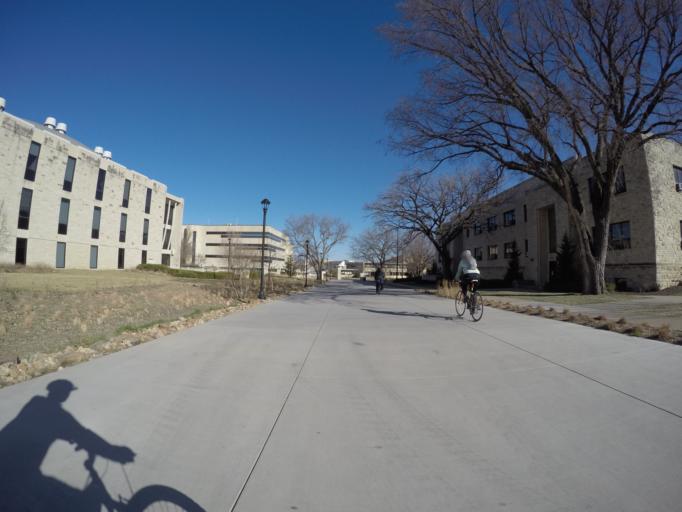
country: US
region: Kansas
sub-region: Riley County
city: Manhattan
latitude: 39.1925
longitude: -96.5835
